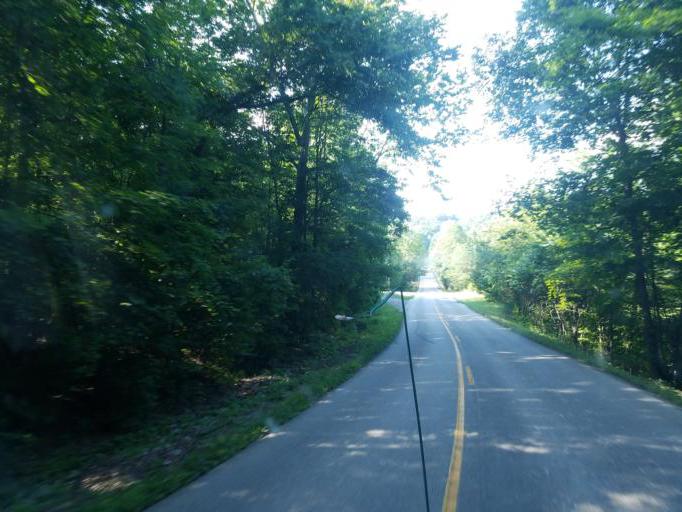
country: US
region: Kentucky
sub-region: Hart County
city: Munfordville
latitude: 37.3313
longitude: -86.0560
